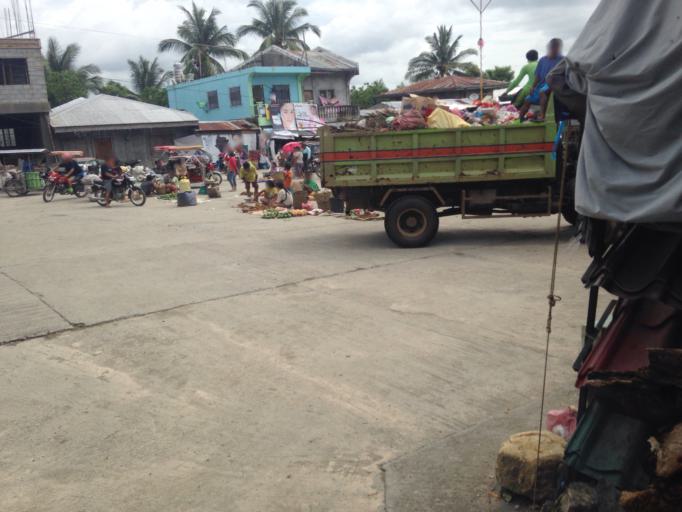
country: PH
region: Mimaropa
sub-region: Province of Mindoro Oriental
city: Bulalacao
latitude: 12.3288
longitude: 121.3436
